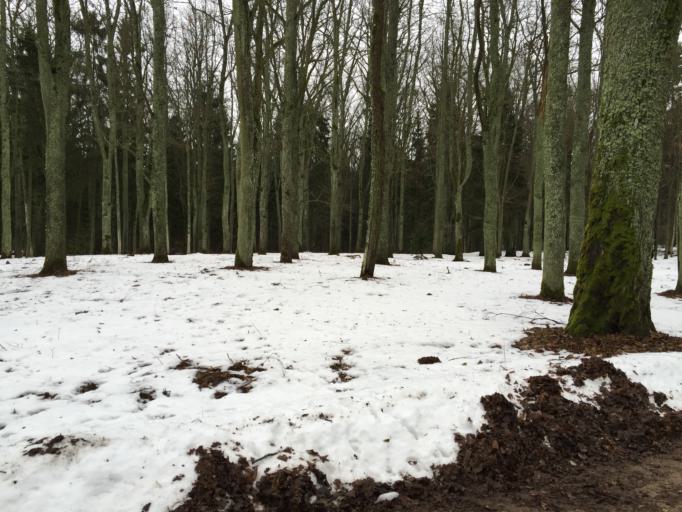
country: LV
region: Krimulda
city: Ragana
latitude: 57.1677
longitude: 24.7211
